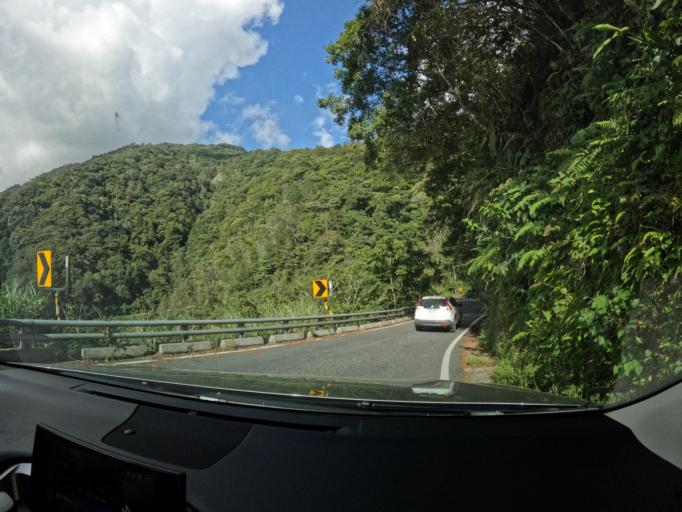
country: TW
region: Taiwan
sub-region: Taitung
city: Taitung
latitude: 23.1981
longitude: 121.0208
